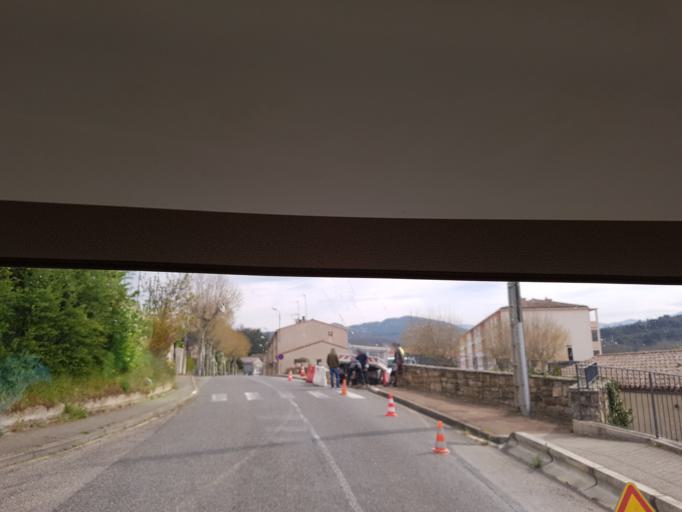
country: FR
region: Languedoc-Roussillon
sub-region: Departement de l'Aude
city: Esperaza
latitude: 42.9331
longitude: 2.2182
